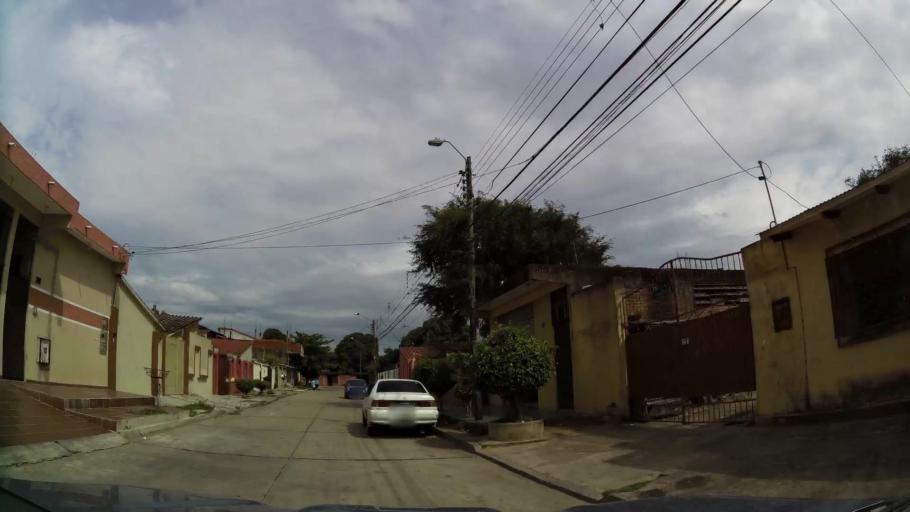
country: BO
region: Santa Cruz
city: Santa Cruz de la Sierra
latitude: -17.7793
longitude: -63.2091
